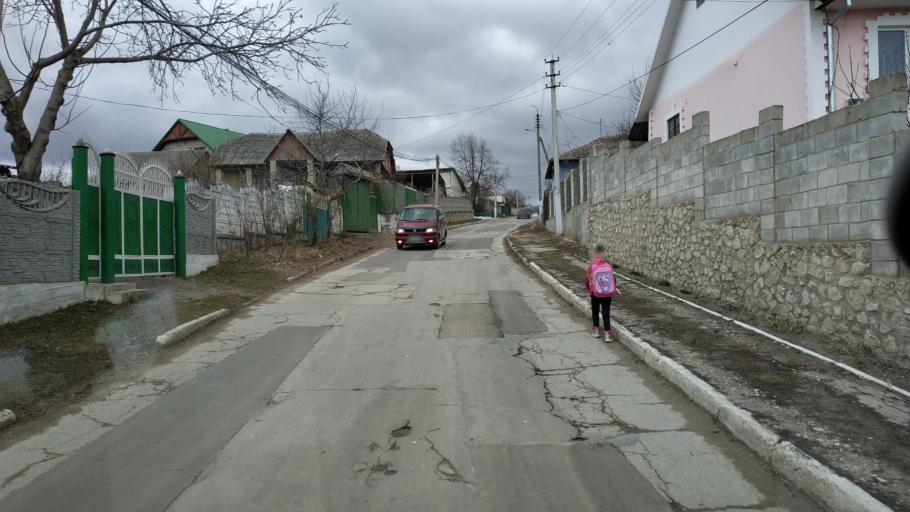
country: MD
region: Stinga Nistrului
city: Bucovat
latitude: 47.2320
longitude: 28.4242
